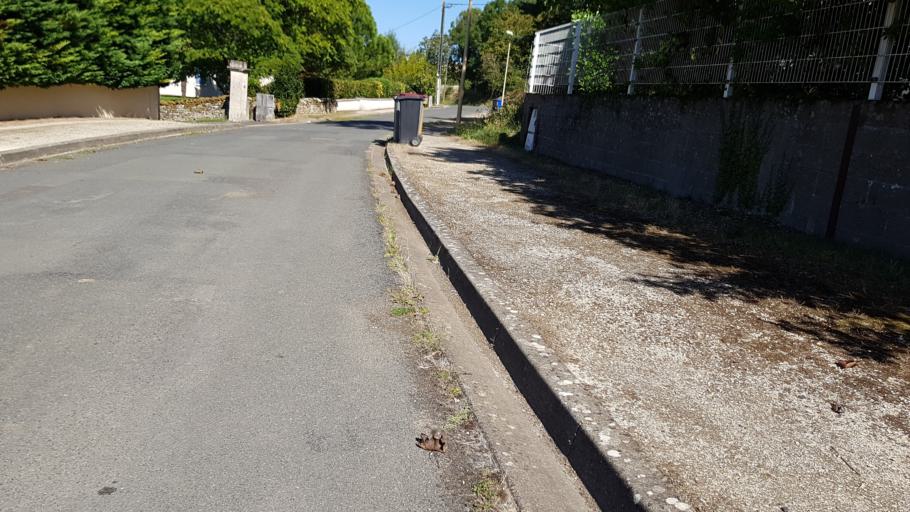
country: FR
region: Poitou-Charentes
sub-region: Departement des Deux-Sevres
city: Vouille
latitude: 46.3143
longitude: -0.3714
